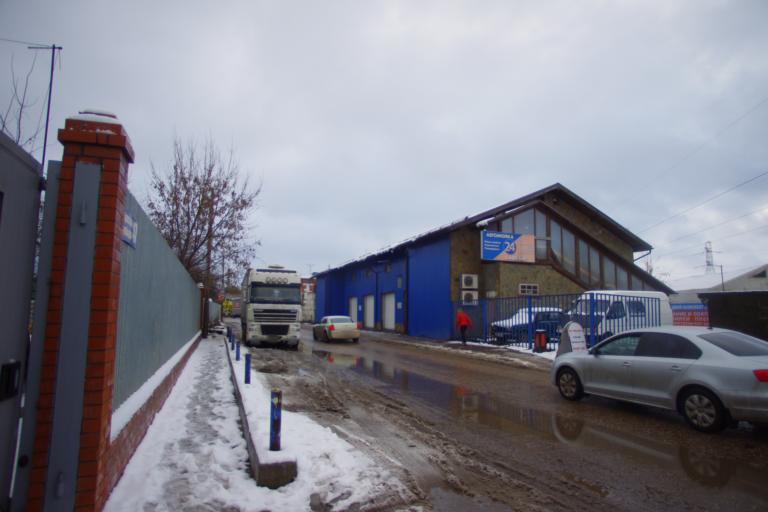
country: RU
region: Moskovskaya
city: Arkhangel'skoye
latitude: 55.8015
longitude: 37.3069
